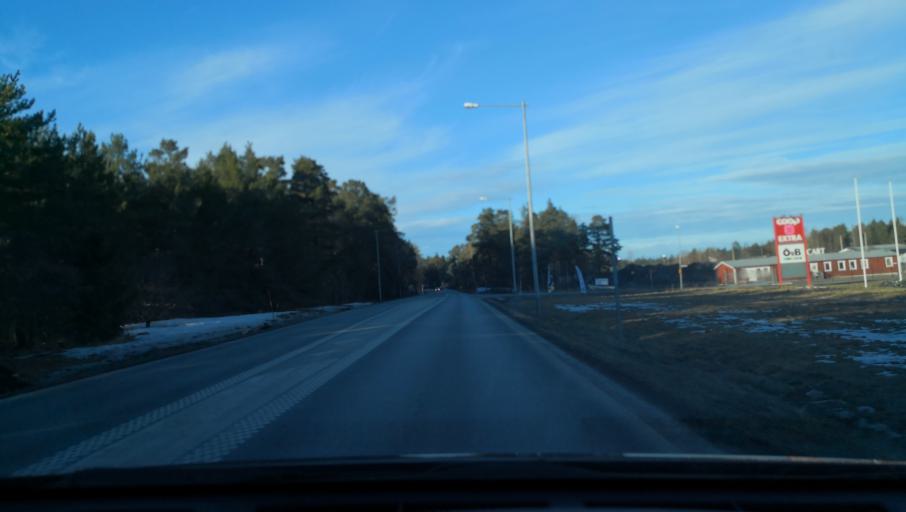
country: SE
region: Uppsala
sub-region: Osthammars Kommun
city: OEsthammar
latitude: 60.2482
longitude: 18.3476
